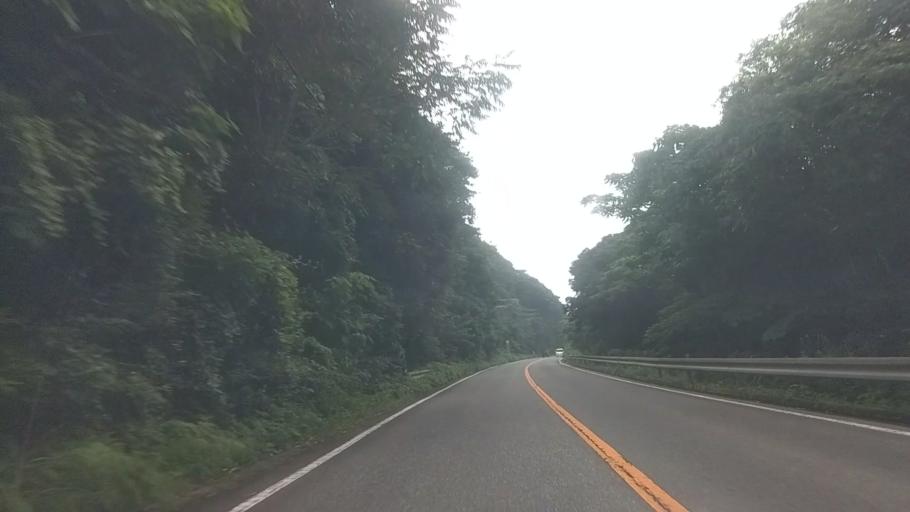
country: JP
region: Chiba
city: Katsuura
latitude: 35.1628
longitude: 140.3201
